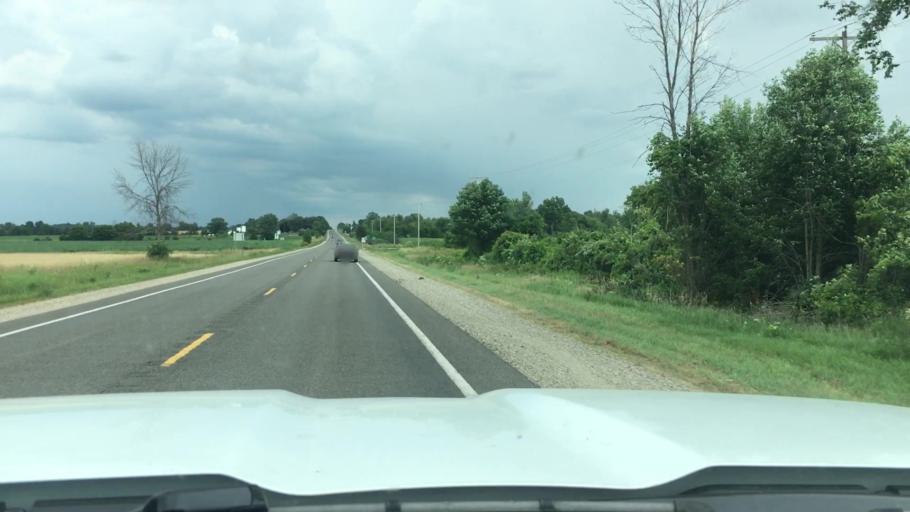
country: US
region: Michigan
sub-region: Montcalm County
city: Carson City
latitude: 43.1776
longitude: -84.9578
